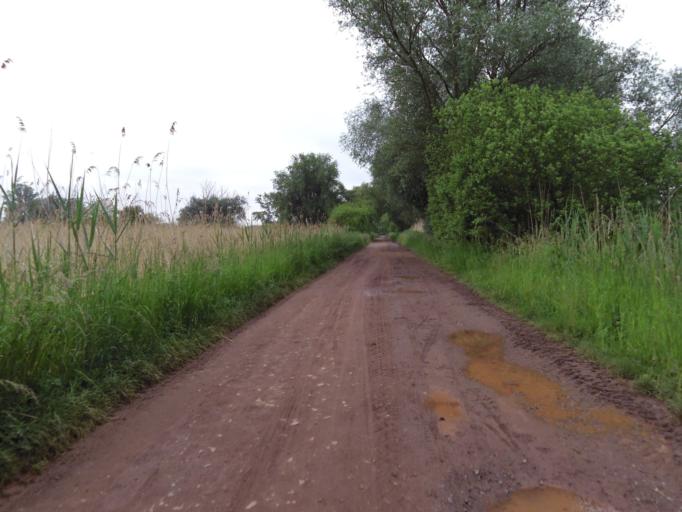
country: DE
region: Rheinland-Pfalz
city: Bobenheim-Roxheim
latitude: 49.5855
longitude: 8.3785
